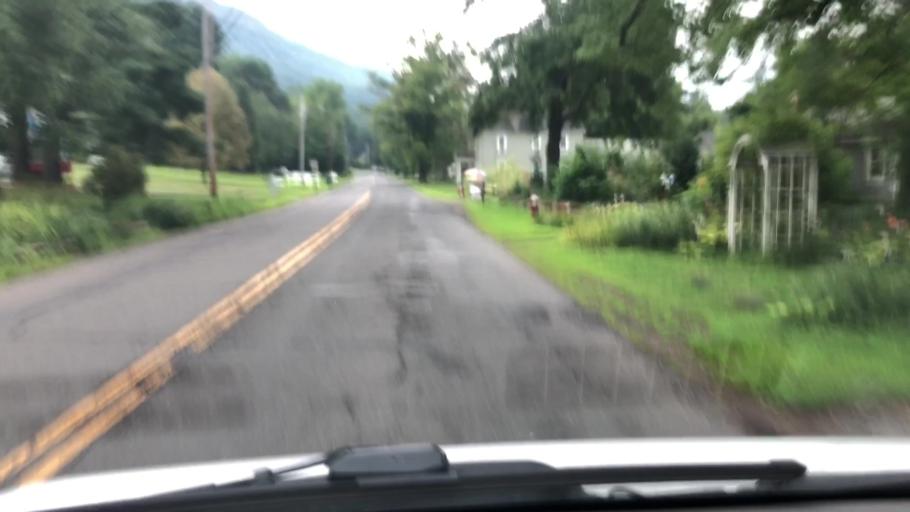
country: US
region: Massachusetts
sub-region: Hampshire County
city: Easthampton
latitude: 42.2645
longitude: -72.6496
